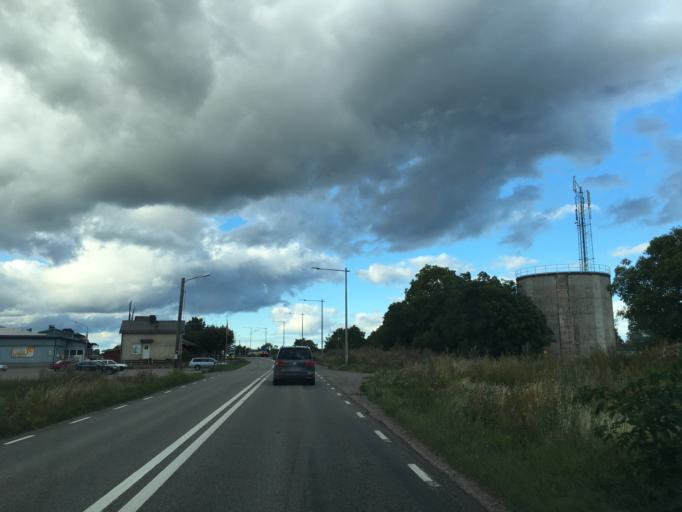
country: SE
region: Kalmar
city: Faerjestaden
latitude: 56.6498
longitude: 16.5177
